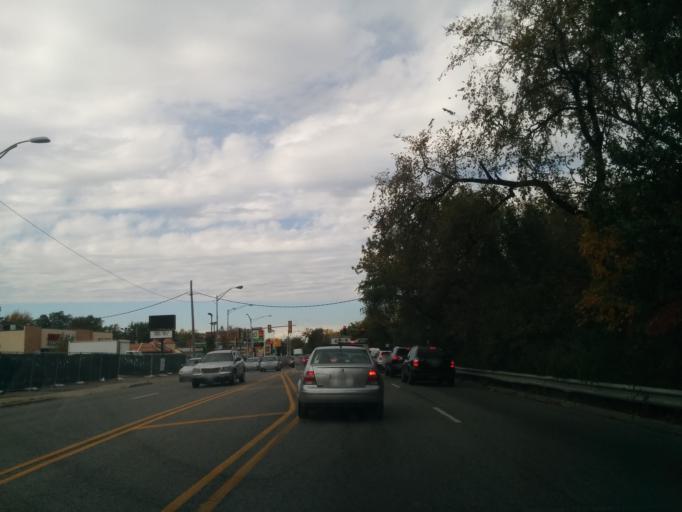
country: US
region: Illinois
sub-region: Cook County
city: River Grove
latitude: 41.9285
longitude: -87.8455
